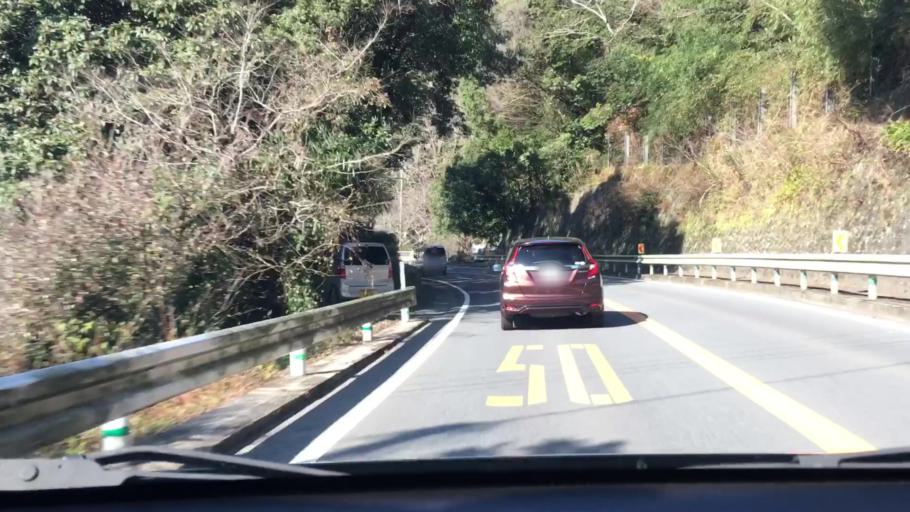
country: JP
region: Oita
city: Saiki
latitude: 32.9943
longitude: 131.8281
